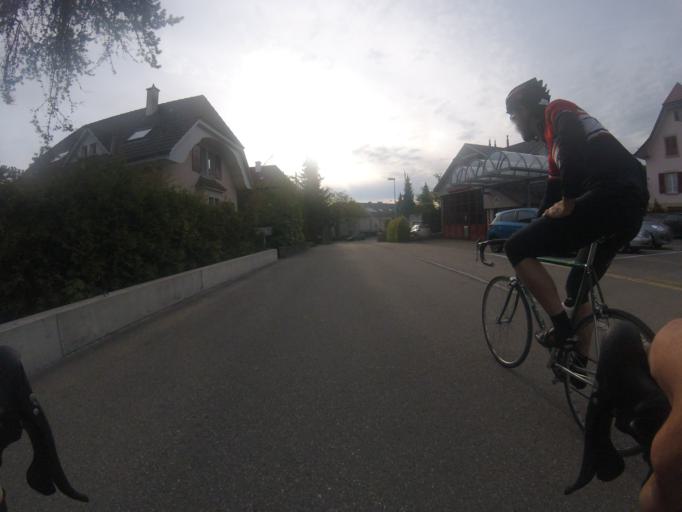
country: CH
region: Bern
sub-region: Bern-Mittelland District
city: Muri
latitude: 46.9347
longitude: 7.5012
